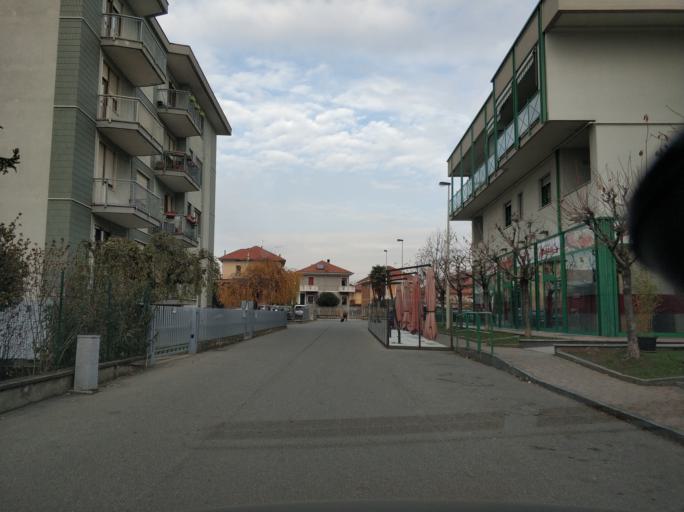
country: IT
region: Piedmont
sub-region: Provincia di Torino
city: Cirie
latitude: 45.2252
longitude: 7.6051
